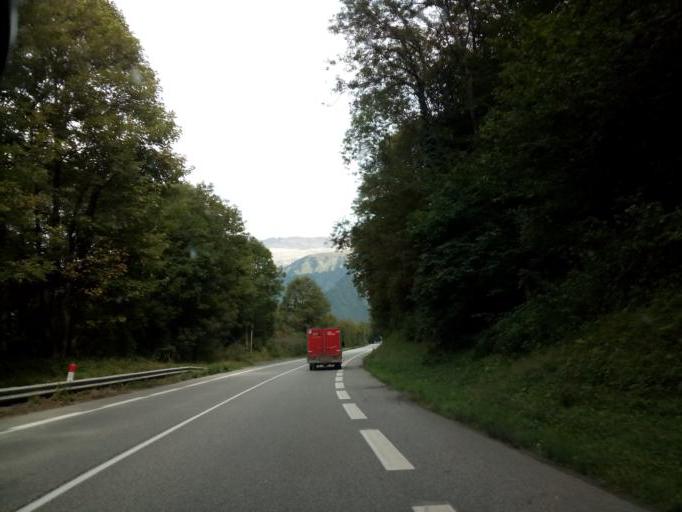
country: FR
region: Rhone-Alpes
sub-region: Departement de l'Isere
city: Livet-et-Gavet
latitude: 45.1183
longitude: 5.9725
